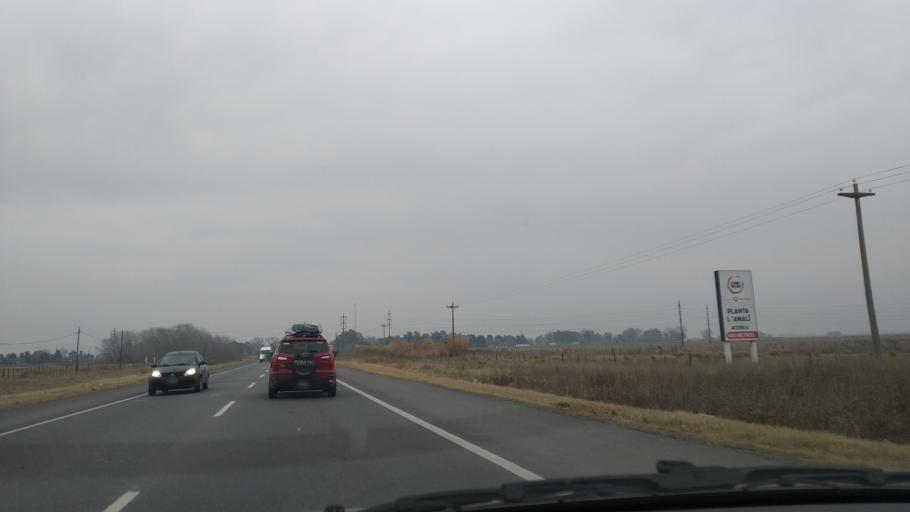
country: AR
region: Buenos Aires
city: Olavarria
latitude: -36.9870
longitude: -60.3011
